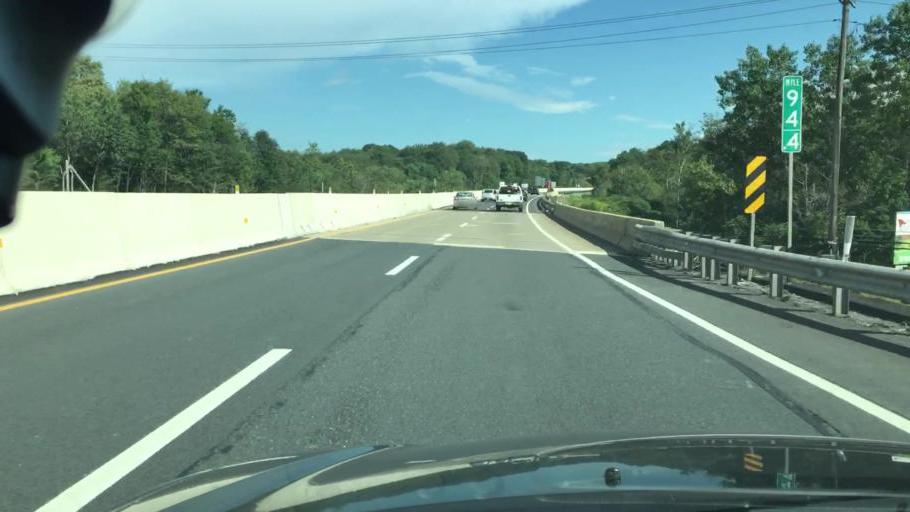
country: US
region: Pennsylvania
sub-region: Luzerne County
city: White Haven
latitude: 41.0718
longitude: -75.7006
